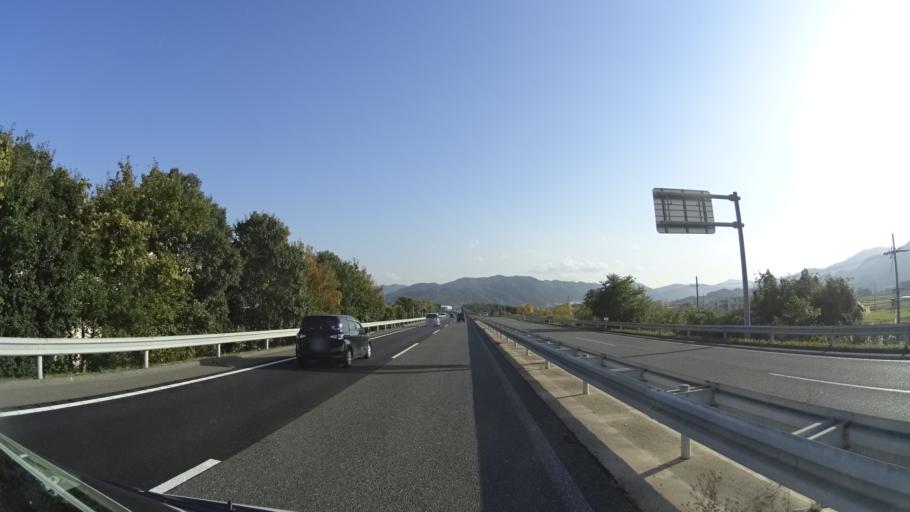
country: JP
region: Kyoto
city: Kameoka
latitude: 35.0262
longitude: 135.5483
